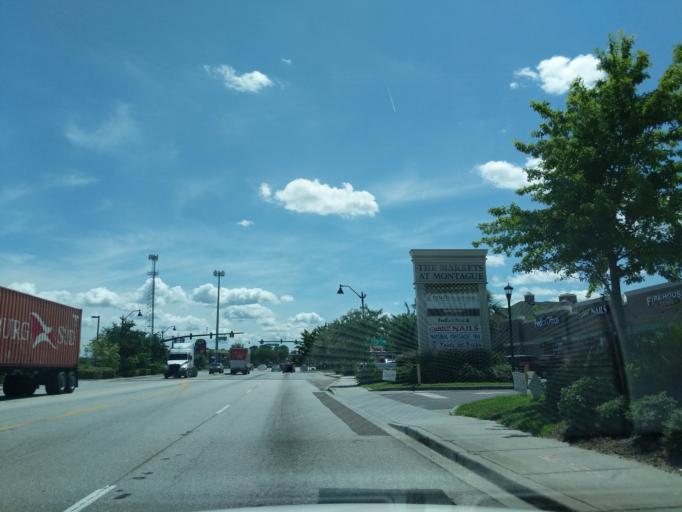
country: US
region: South Carolina
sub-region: Charleston County
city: North Charleston
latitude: 32.8669
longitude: -80.0134
